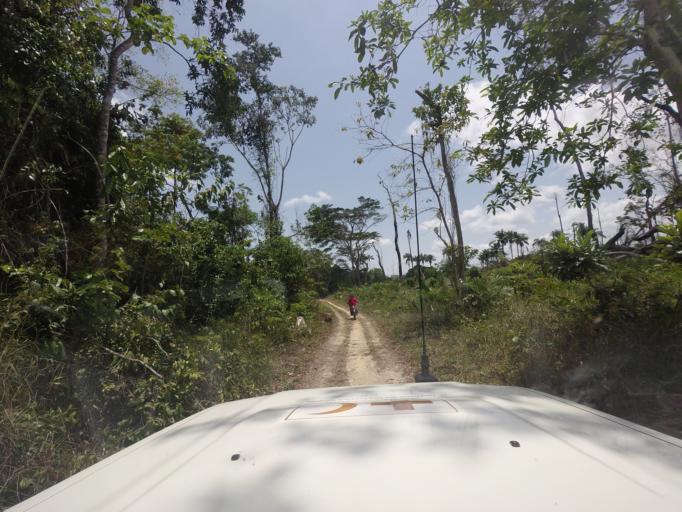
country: GN
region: Nzerekore
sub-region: Yomou
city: Yomou
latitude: 7.3757
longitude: -9.3081
